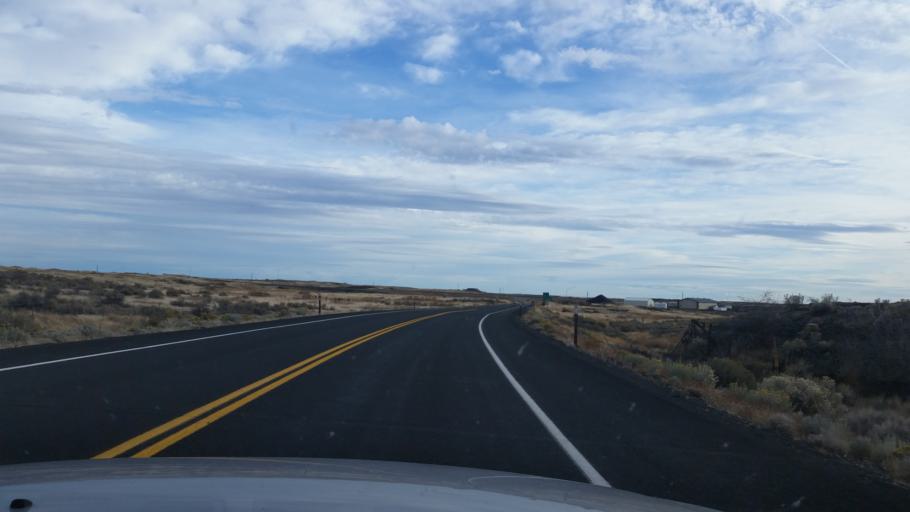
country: US
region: Washington
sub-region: Lincoln County
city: Davenport
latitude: 47.3153
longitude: -117.9739
